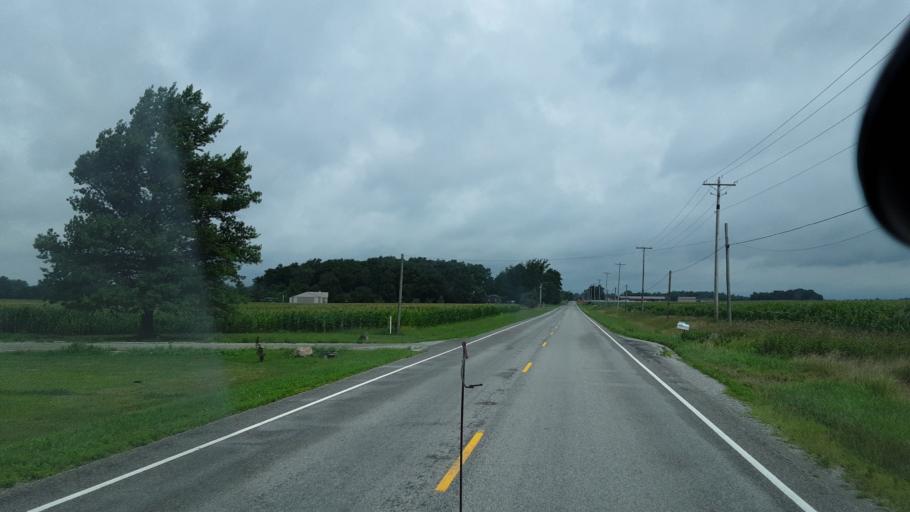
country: US
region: Indiana
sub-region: Allen County
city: Monroeville
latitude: 40.9553
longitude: -84.8624
